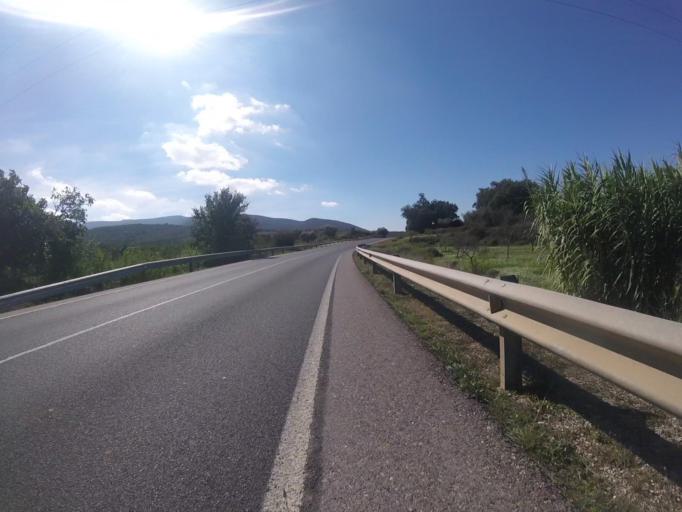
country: ES
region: Valencia
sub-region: Provincia de Castello
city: Sarratella
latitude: 40.3291
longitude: -0.0160
